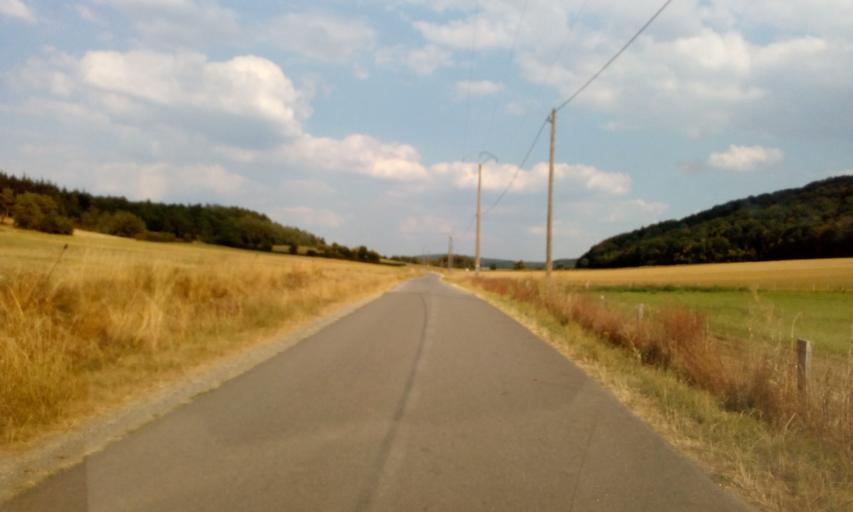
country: BE
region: Wallonia
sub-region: Province du Luxembourg
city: Tellin
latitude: 50.1112
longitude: 5.1736
